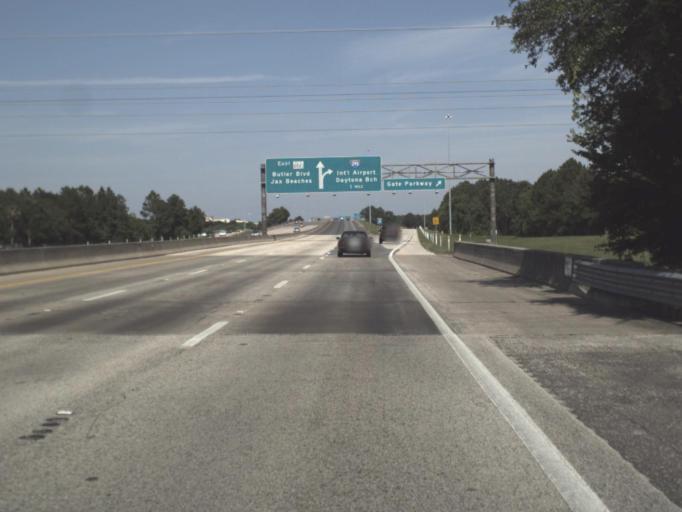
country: US
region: Florida
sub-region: Duval County
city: Jacksonville
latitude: 30.2499
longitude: -81.5426
